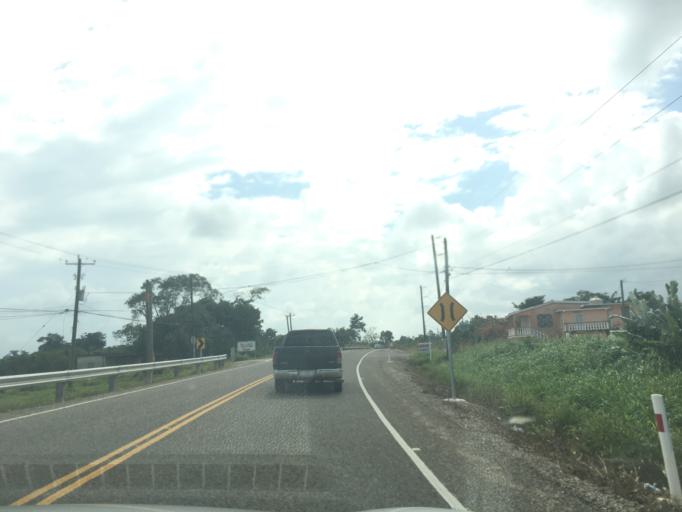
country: BZ
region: Stann Creek
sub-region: Dangriga
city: Dangriga
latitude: 17.0011
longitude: -88.3027
